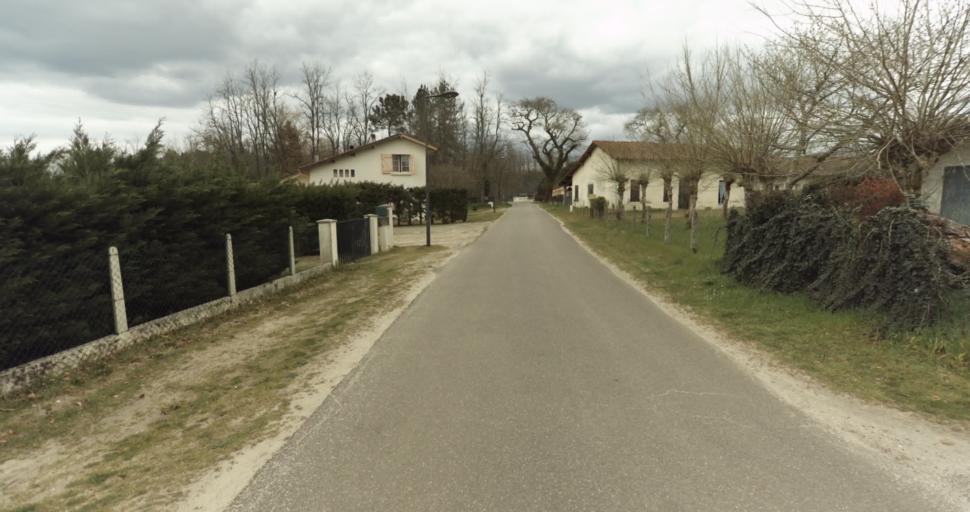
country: FR
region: Aquitaine
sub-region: Departement des Landes
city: Roquefort
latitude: 44.0357
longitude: -0.3093
